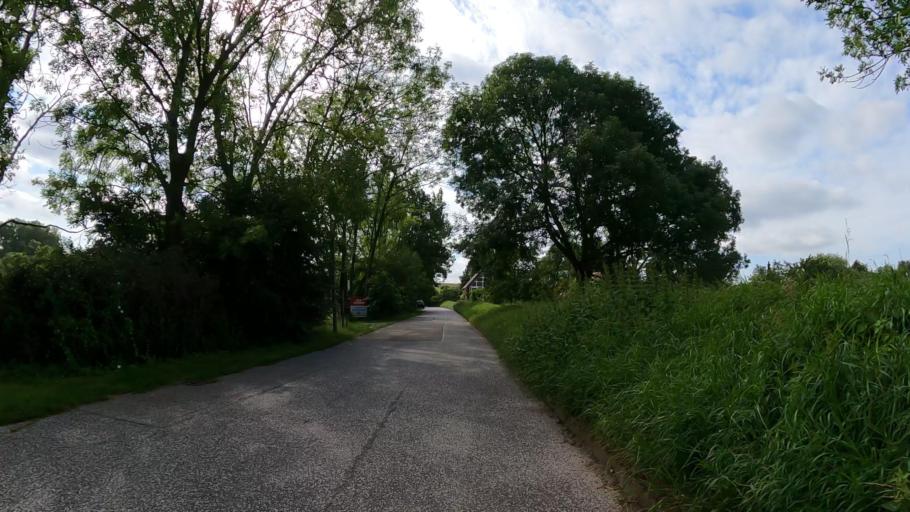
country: DE
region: Hamburg
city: Altona
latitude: 53.5216
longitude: 9.8670
